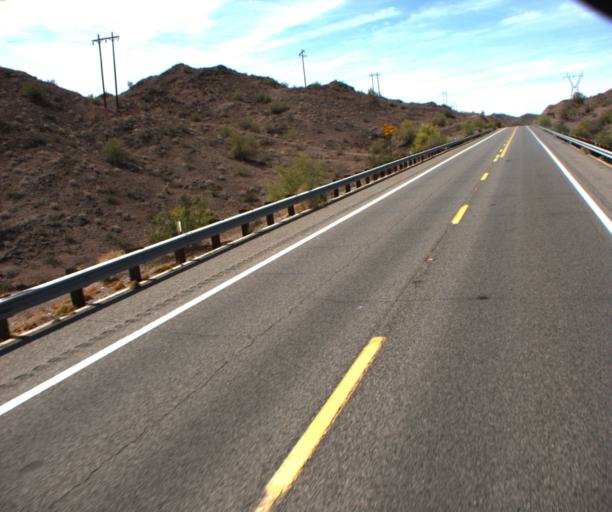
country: US
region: Arizona
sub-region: La Paz County
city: Cienega Springs
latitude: 34.3459
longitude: -114.1495
